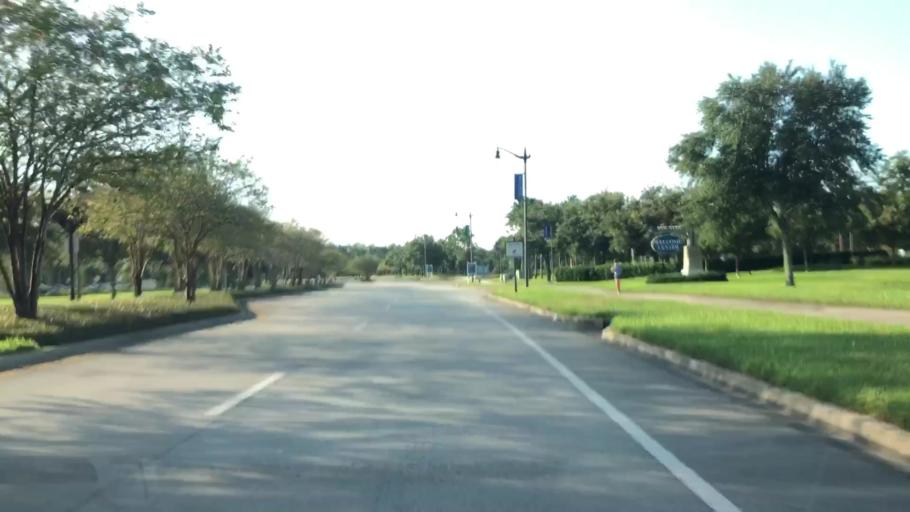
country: US
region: Florida
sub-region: Saint Johns County
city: Palm Valley
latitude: 30.1041
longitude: -81.4150
